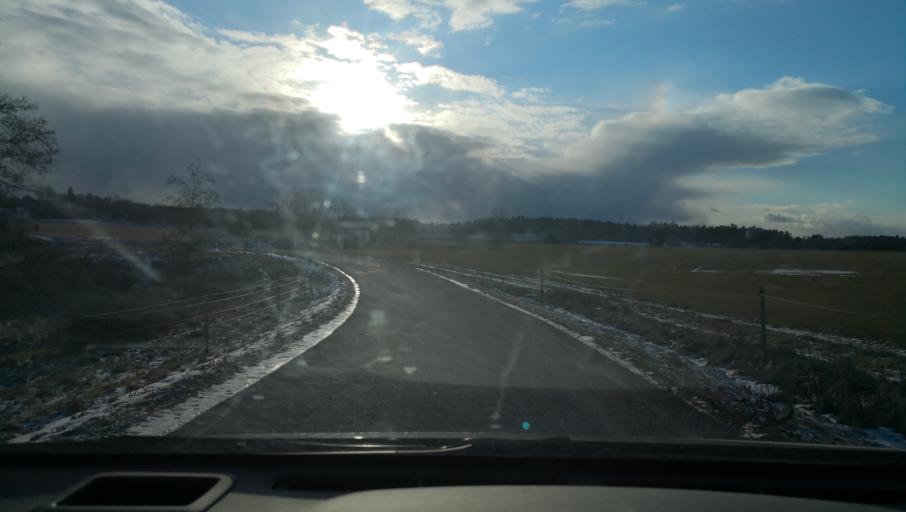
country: SE
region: Uppsala
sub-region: Enkopings Kommun
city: Irsta
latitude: 59.6599
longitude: 16.8081
